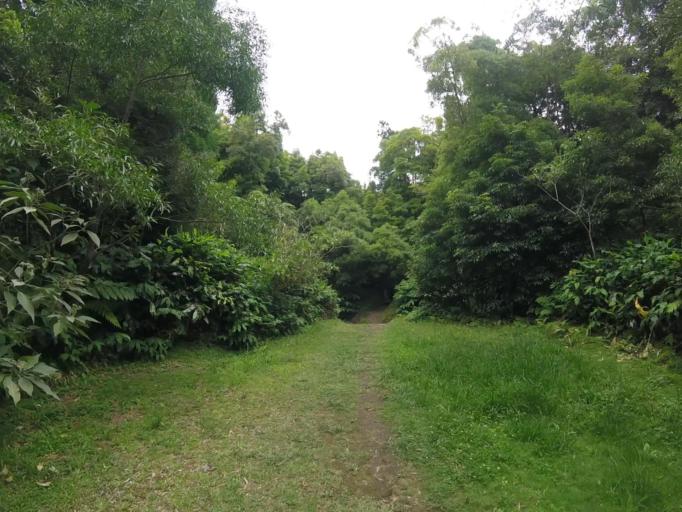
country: PT
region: Azores
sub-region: Vila Franca do Campo
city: Vila Franca do Campo
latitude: 37.7459
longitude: -25.5141
